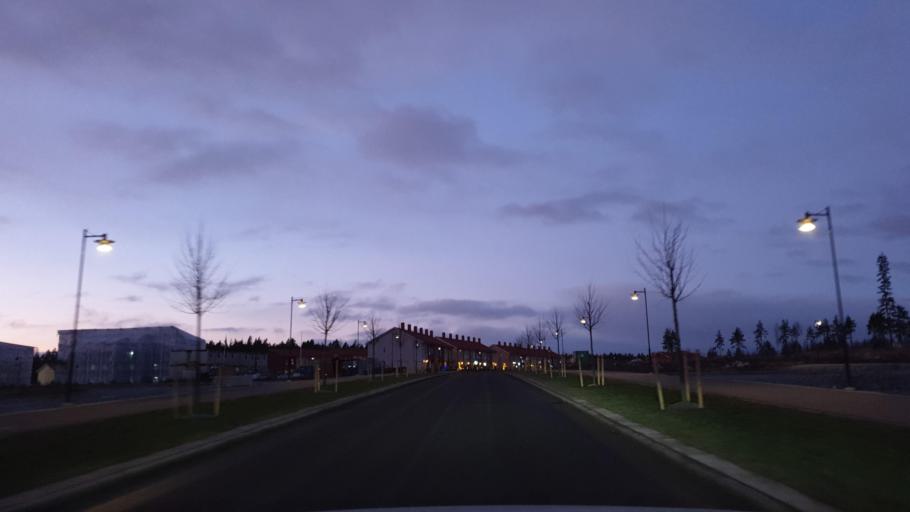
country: SE
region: Stockholm
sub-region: Sigtuna Kommun
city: Marsta
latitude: 59.6076
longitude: 17.7972
